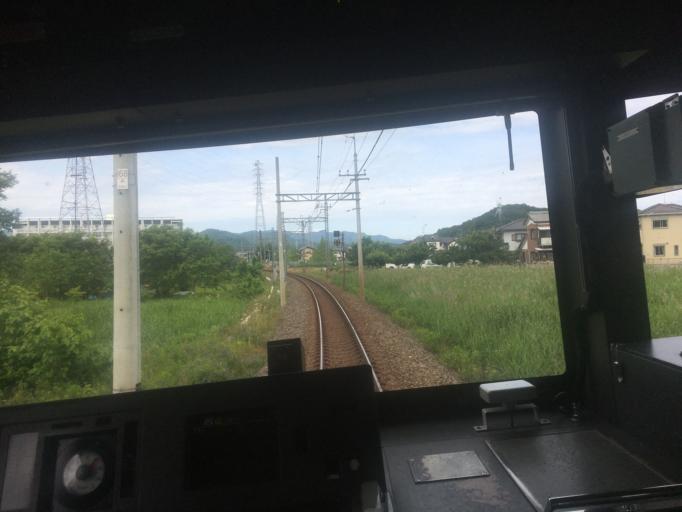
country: JP
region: Saitama
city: Ogawa
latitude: 36.0565
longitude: 139.2757
